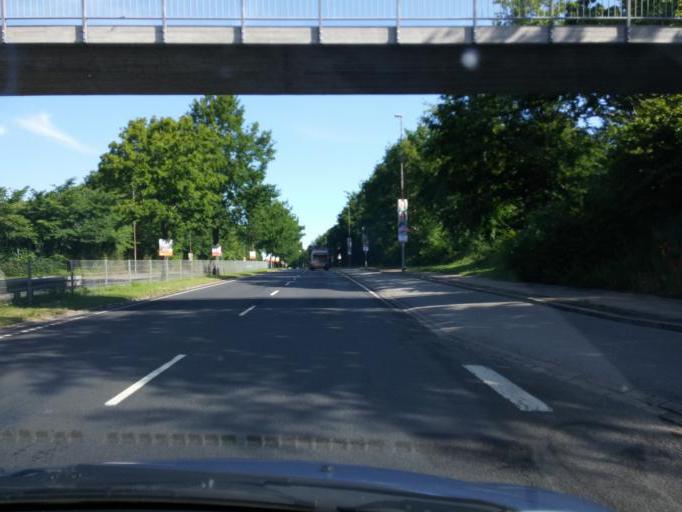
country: DK
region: South Denmark
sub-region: Odense Kommune
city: Seden
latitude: 55.4102
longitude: 10.4246
